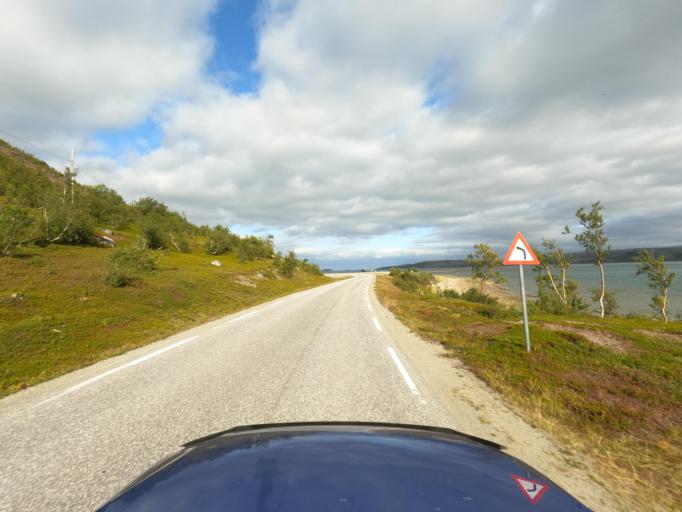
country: NO
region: Finnmark Fylke
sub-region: Porsanger
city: Lakselv
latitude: 70.1026
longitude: 24.9152
